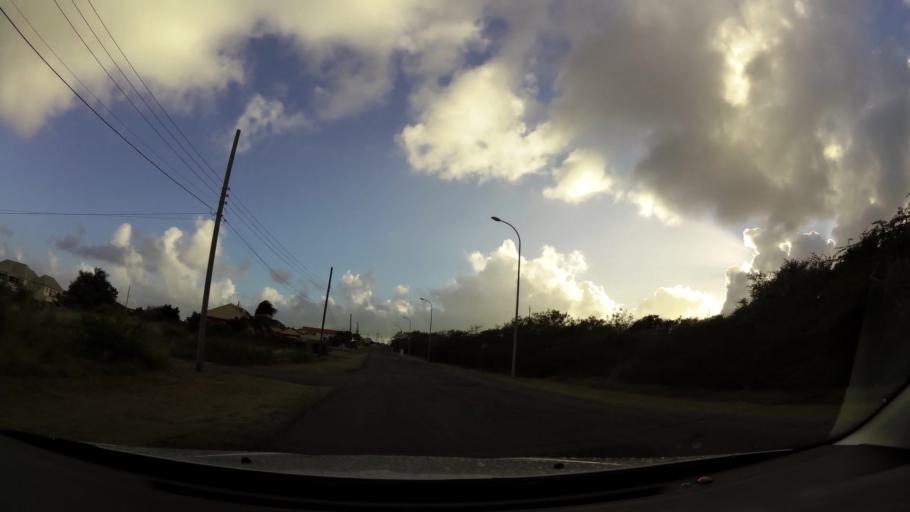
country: AG
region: Saint John
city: Saint John's
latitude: 17.1553
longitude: -61.8288
